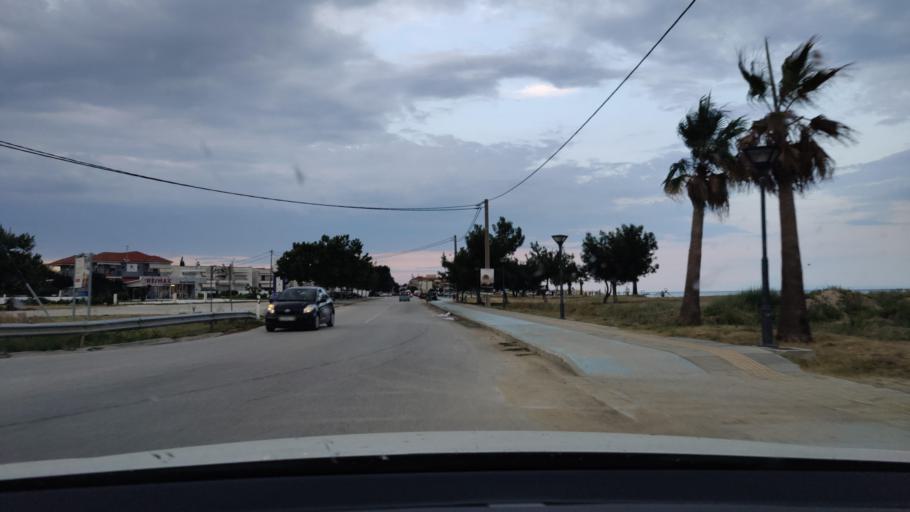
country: GR
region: East Macedonia and Thrace
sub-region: Nomos Kavalas
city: Paralia Ofryniou
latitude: 40.7670
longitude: 23.8966
